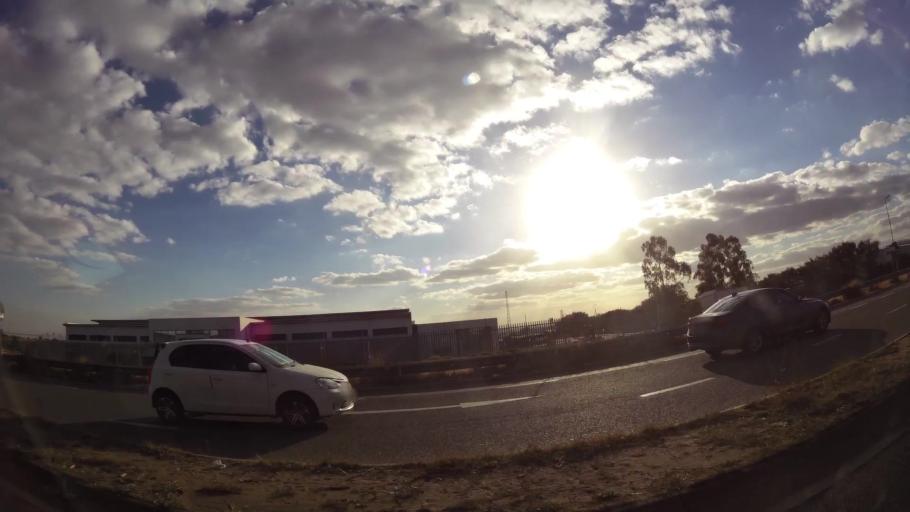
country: ZA
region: Gauteng
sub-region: City of Tshwane Metropolitan Municipality
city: Centurion
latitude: -25.9153
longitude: 28.1637
